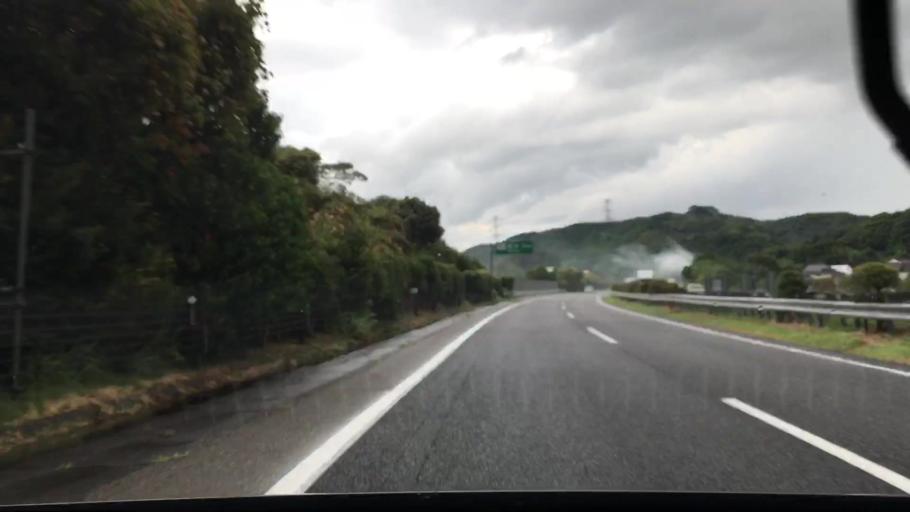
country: JP
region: Fukuoka
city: Nakama
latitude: 33.7675
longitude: 130.6719
